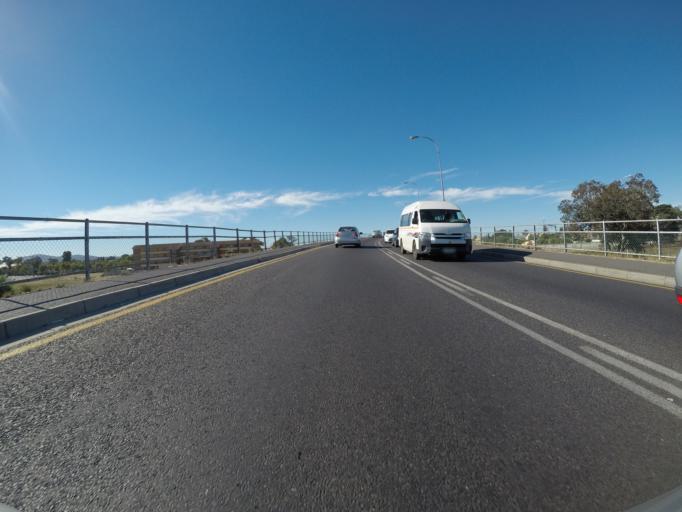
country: ZA
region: Western Cape
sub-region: City of Cape Town
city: Kraaifontein
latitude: -33.9329
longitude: 18.6758
